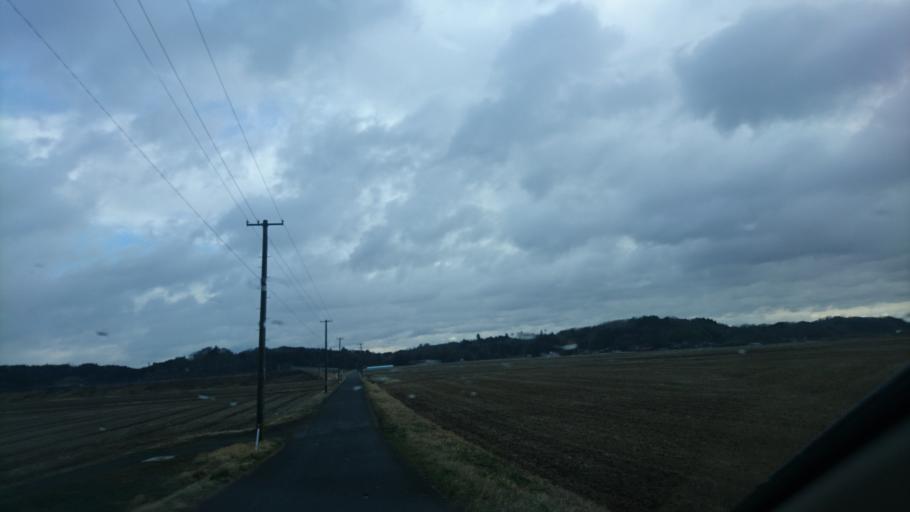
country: JP
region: Iwate
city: Ichinoseki
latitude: 38.7781
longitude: 141.0303
